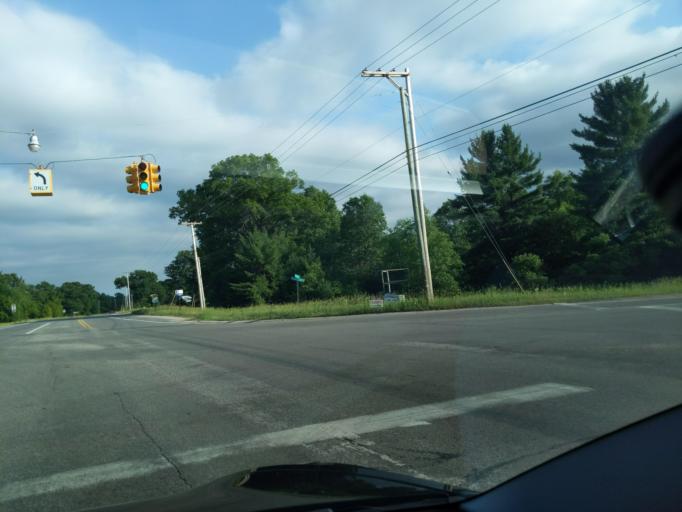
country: US
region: Michigan
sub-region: Muskegon County
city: Lakewood Club
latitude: 43.3843
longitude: -86.2886
